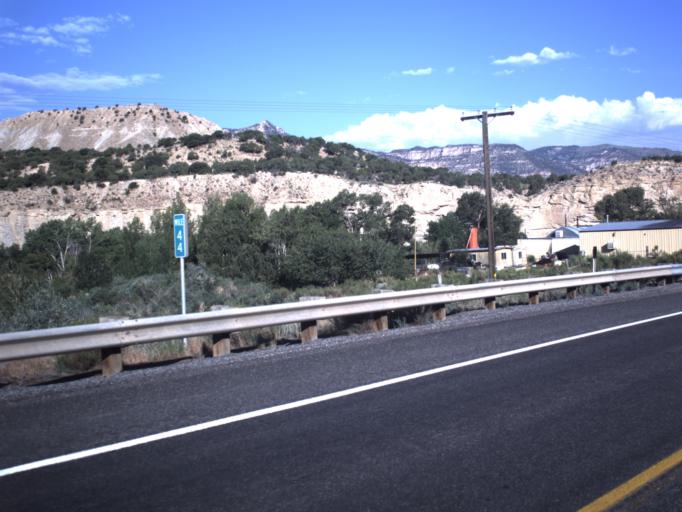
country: US
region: Utah
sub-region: Emery County
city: Huntington
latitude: 39.3563
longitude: -111.0280
